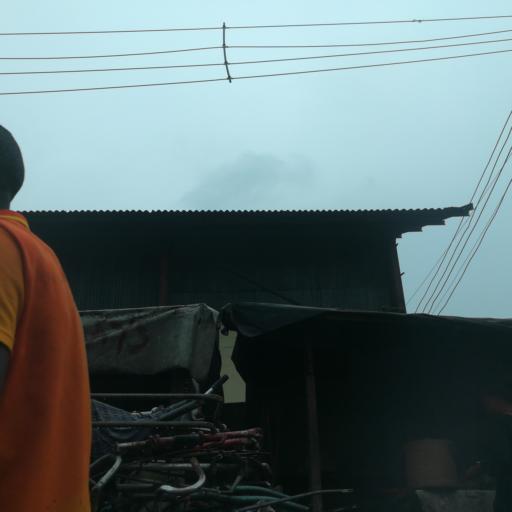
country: NG
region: Rivers
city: Port Harcourt
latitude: 4.7942
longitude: 6.9969
